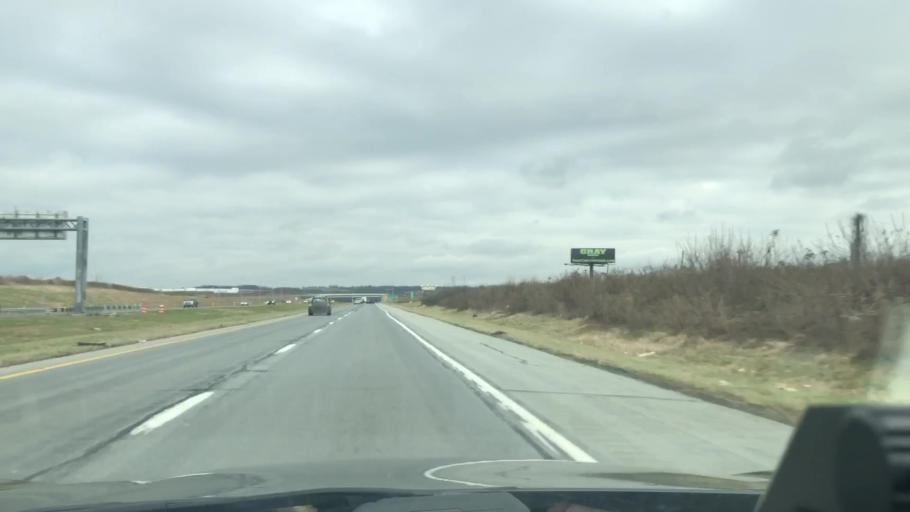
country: US
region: Pennsylvania
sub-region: Northampton County
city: Tatamy
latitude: 40.7320
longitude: -75.2713
